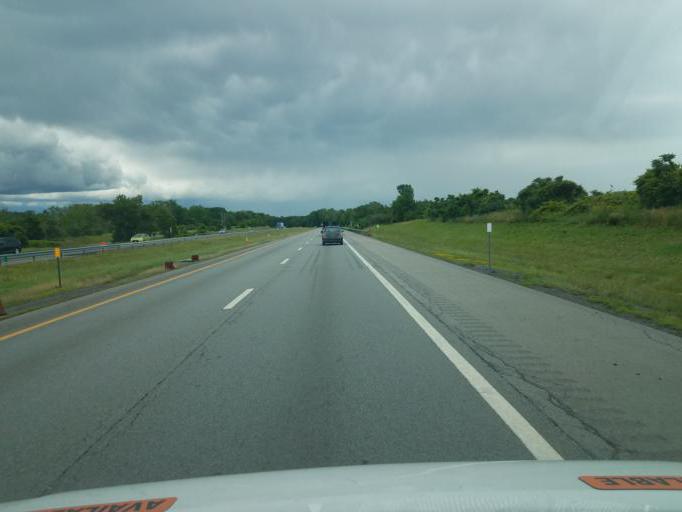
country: US
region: New York
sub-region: Ontario County
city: Phelps
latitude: 42.9604
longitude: -77.0388
